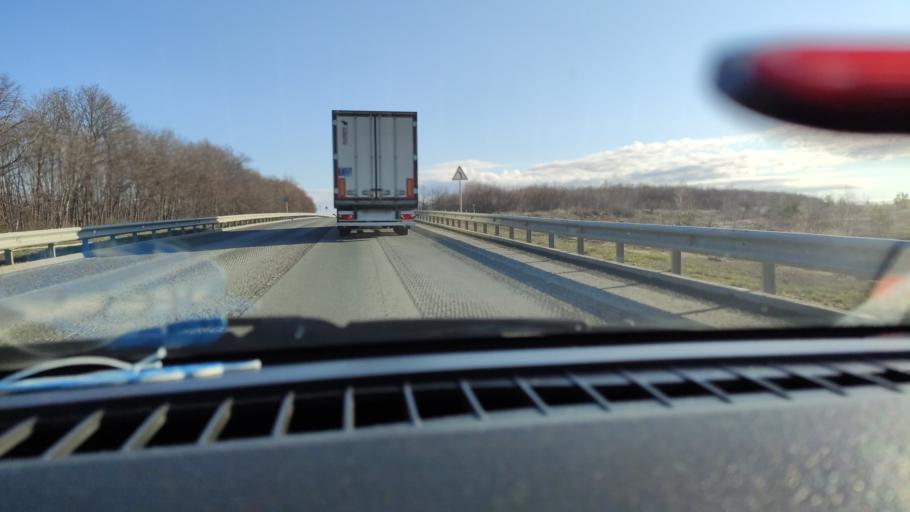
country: RU
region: Saratov
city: Dukhovnitskoye
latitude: 52.7085
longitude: 48.2632
